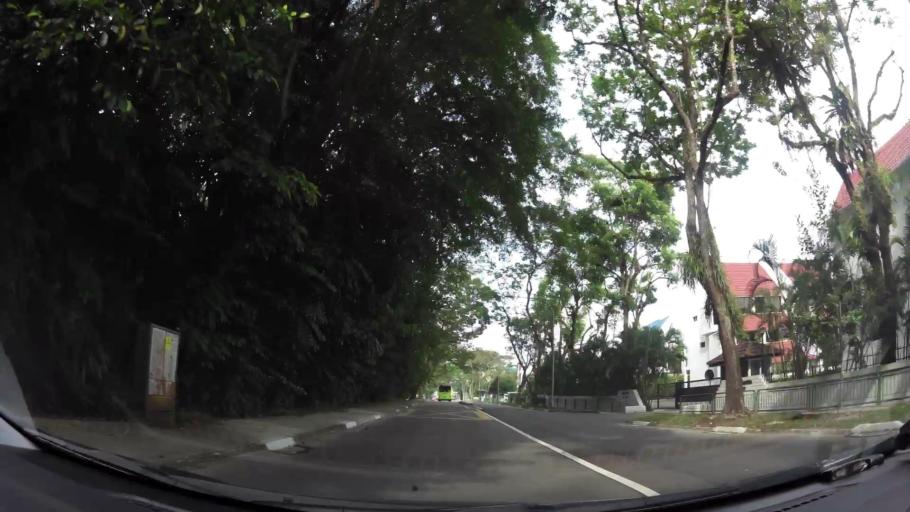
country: SG
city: Singapore
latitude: 1.3234
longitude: 103.7916
